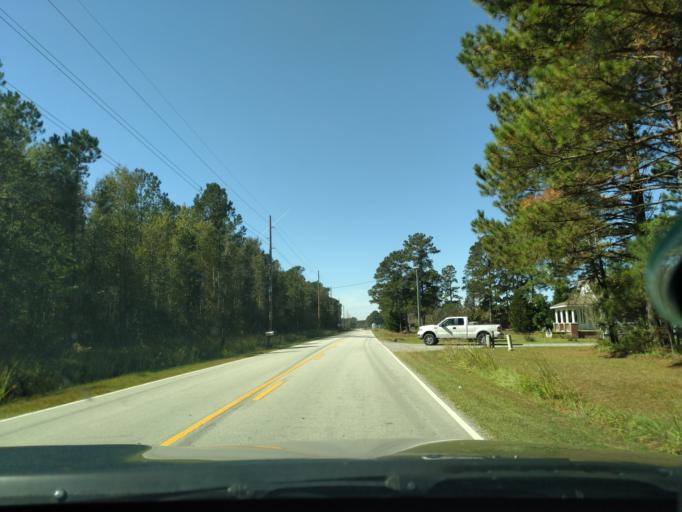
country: US
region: North Carolina
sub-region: Beaufort County
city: River Road
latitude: 35.5782
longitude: -76.9531
